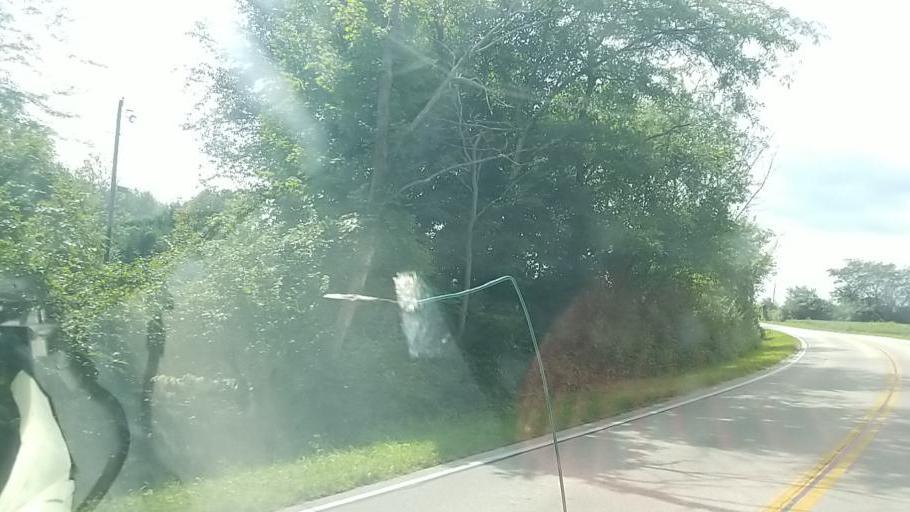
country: US
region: Ohio
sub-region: Pickaway County
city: Commercial Point
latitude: 39.7661
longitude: -83.1594
